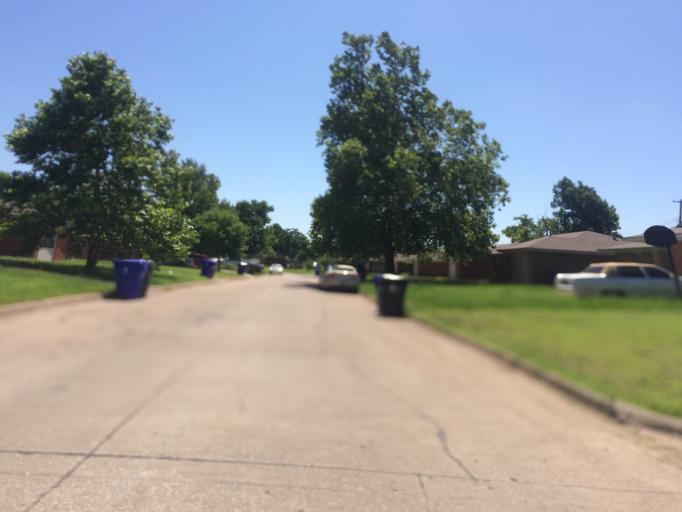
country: US
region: Oklahoma
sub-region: Cleveland County
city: Norman
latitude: 35.2371
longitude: -97.4466
